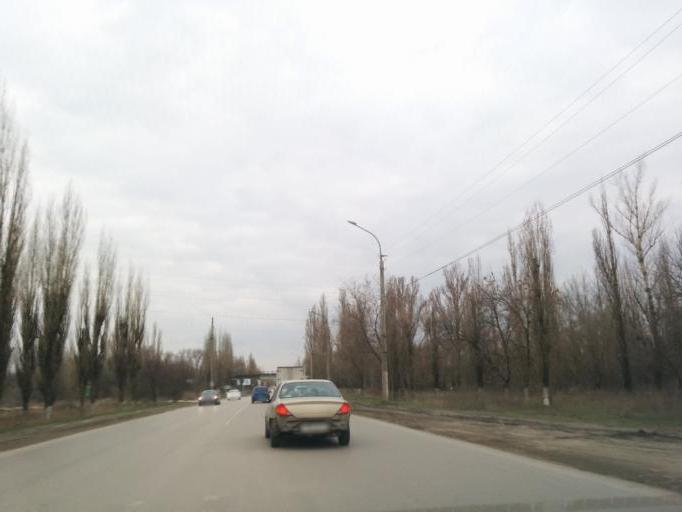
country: RU
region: Rostov
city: Novocherkassk
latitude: 47.4803
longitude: 40.1029
